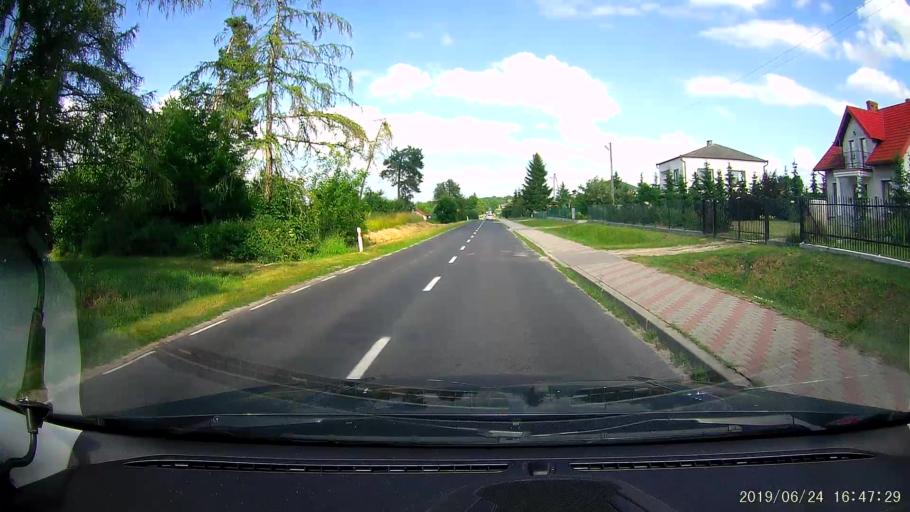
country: PL
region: Lublin Voivodeship
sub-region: Powiat tomaszowski
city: Laszczow
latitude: 50.5302
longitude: 23.7004
